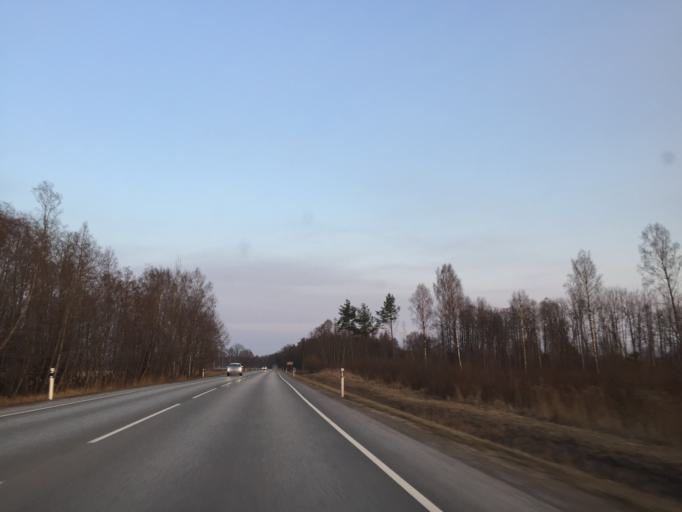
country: EE
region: Paernumaa
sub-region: Audru vald
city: Audru
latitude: 58.4091
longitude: 24.3901
